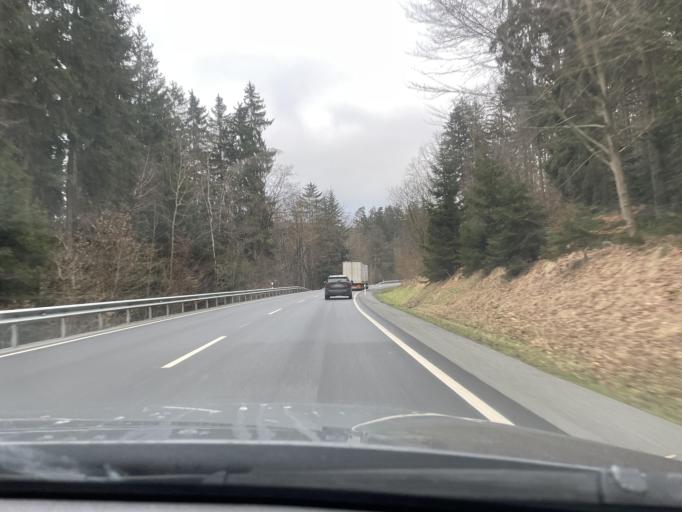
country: DE
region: Bavaria
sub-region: Upper Palatinate
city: Chamerau
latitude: 49.1779
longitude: 12.7512
